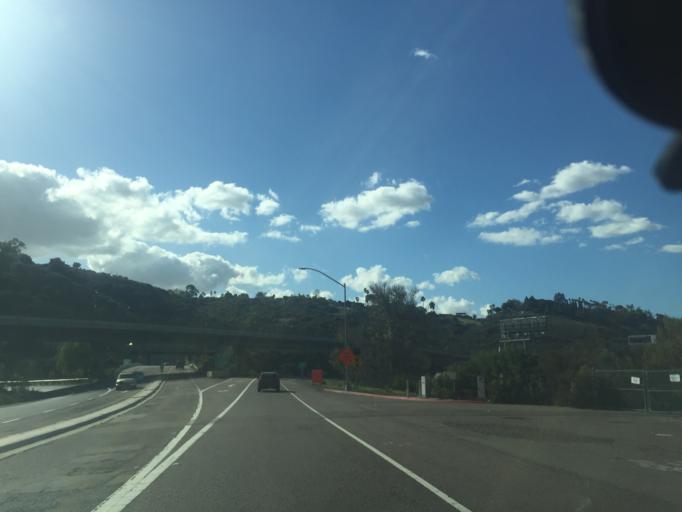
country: US
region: California
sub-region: San Diego County
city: La Mesa
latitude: 32.7828
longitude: -117.0870
